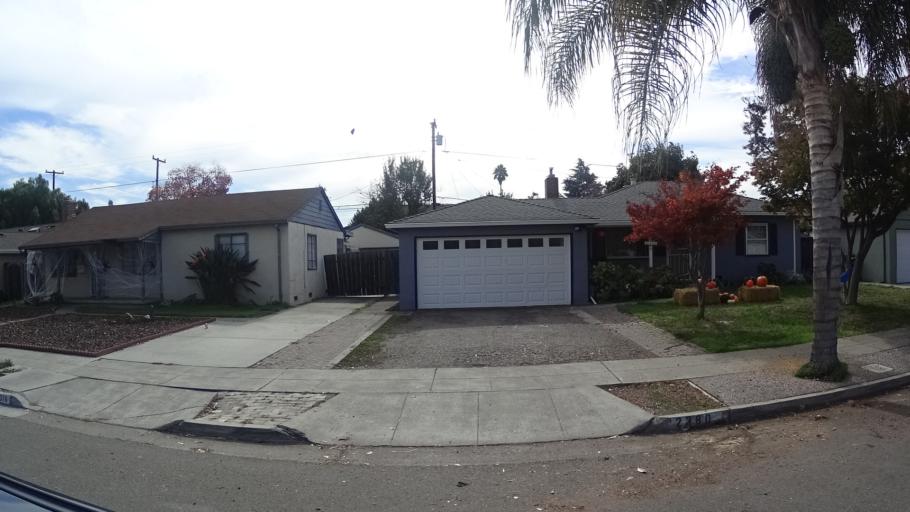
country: US
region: California
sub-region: Santa Clara County
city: Santa Clara
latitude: 37.3369
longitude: -121.9465
